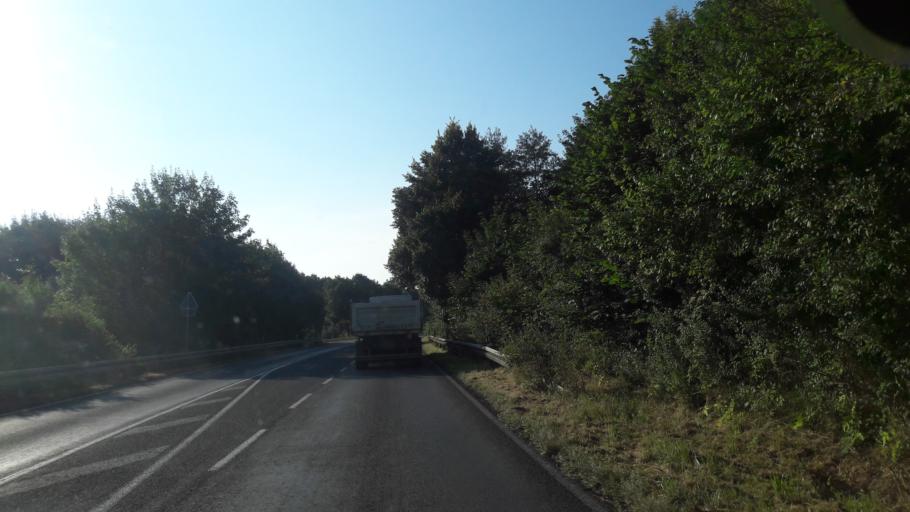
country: DE
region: Lower Saxony
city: Diekholzen
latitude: 52.1308
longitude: 9.8827
